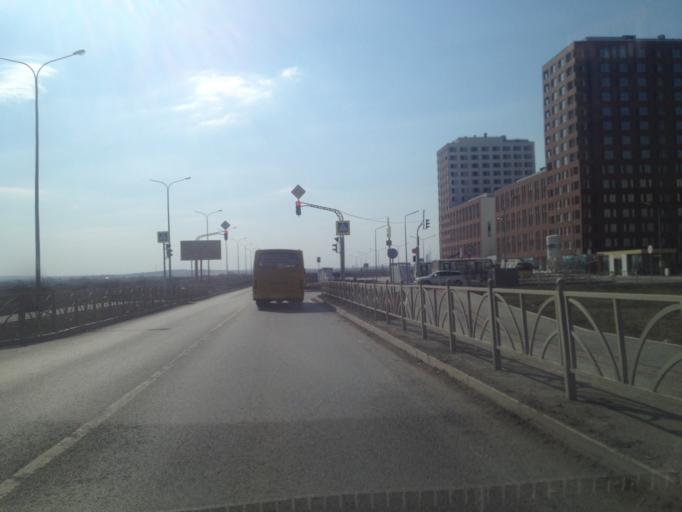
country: RU
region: Sverdlovsk
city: Sovkhoznyy
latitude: 56.7448
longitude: 60.5704
